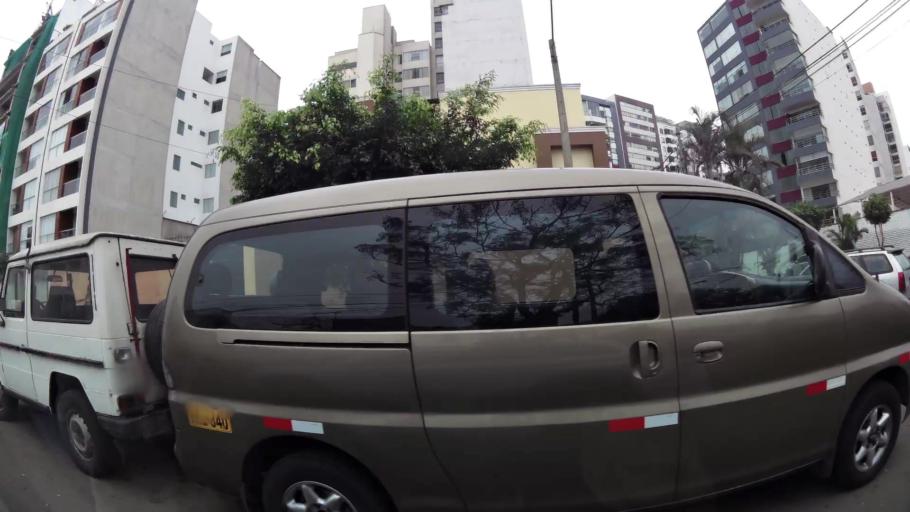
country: PE
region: Lima
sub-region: Lima
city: Surco
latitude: -12.1194
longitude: -77.0162
